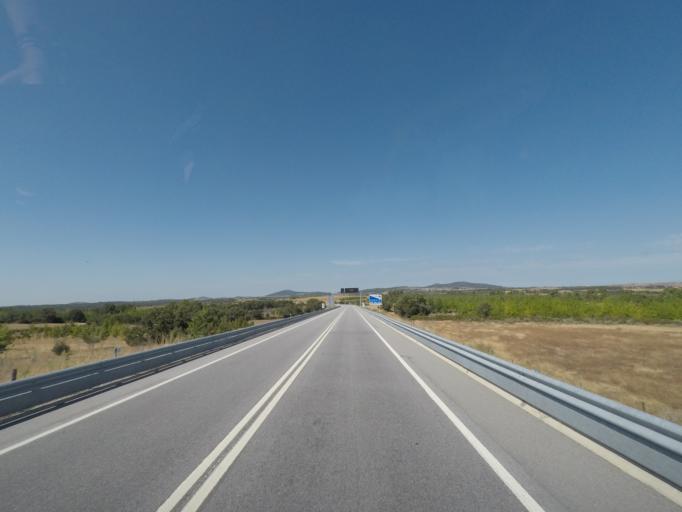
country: ES
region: Castille and Leon
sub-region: Provincia de Salamanca
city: Villarino de los Aires
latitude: 41.3686
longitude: -6.5096
